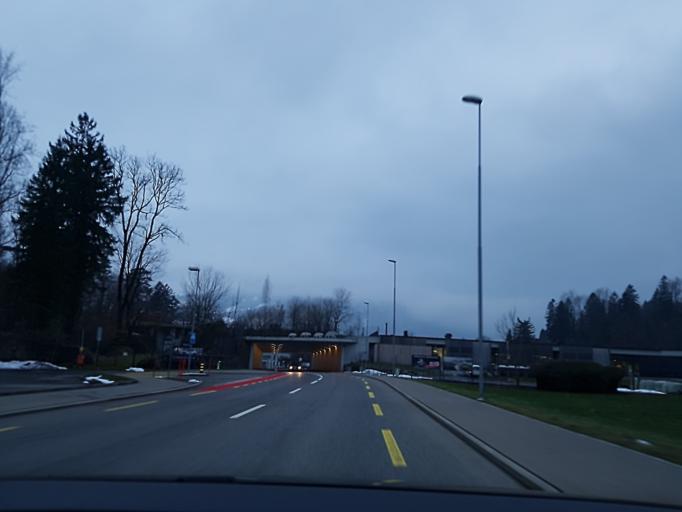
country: CH
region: Schwyz
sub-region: Bezirk Schwyz
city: Goldau
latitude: 47.0528
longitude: 8.5586
